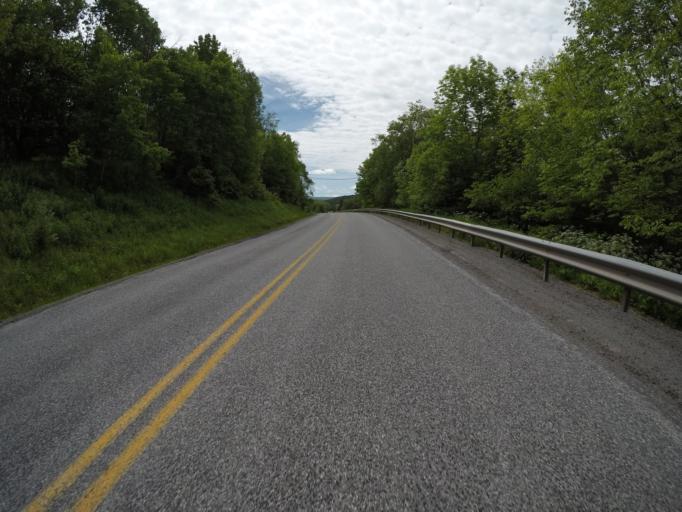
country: US
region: New York
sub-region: Delaware County
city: Stamford
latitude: 42.2297
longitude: -74.5626
